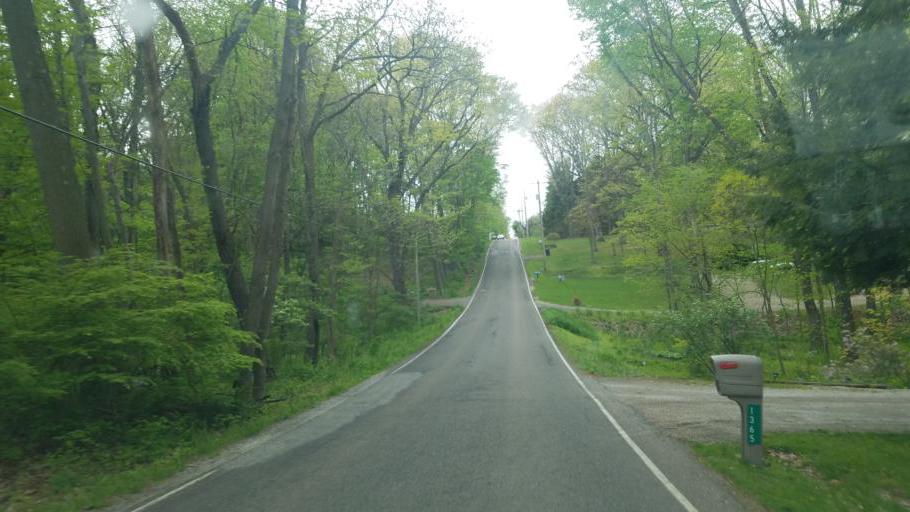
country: US
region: Ohio
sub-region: Knox County
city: Mount Vernon
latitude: 40.3915
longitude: -82.4502
